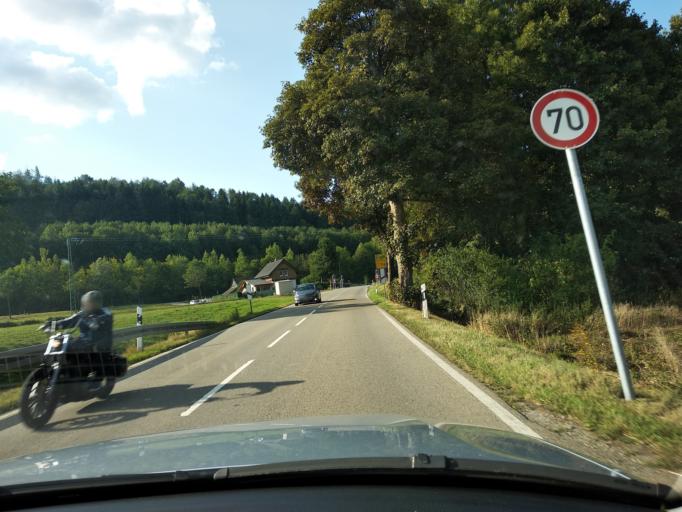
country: DE
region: Baden-Wuerttemberg
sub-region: Tuebingen Region
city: Aichstetten
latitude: 47.8767
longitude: 10.0372
